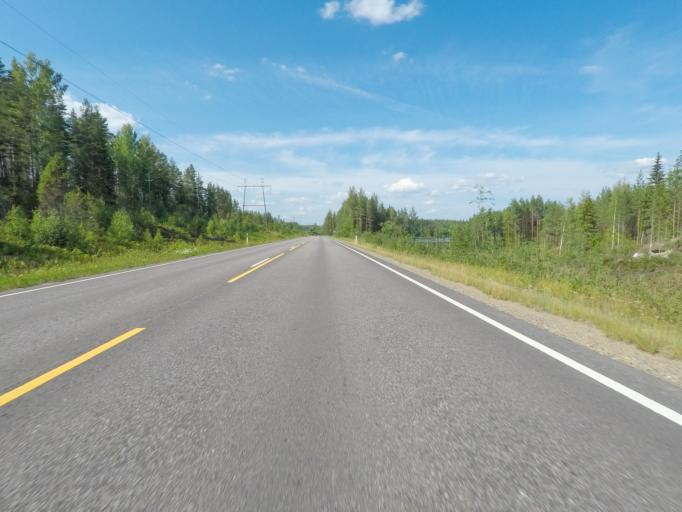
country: FI
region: Southern Savonia
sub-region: Mikkeli
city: Puumala
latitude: 61.5583
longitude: 28.1807
